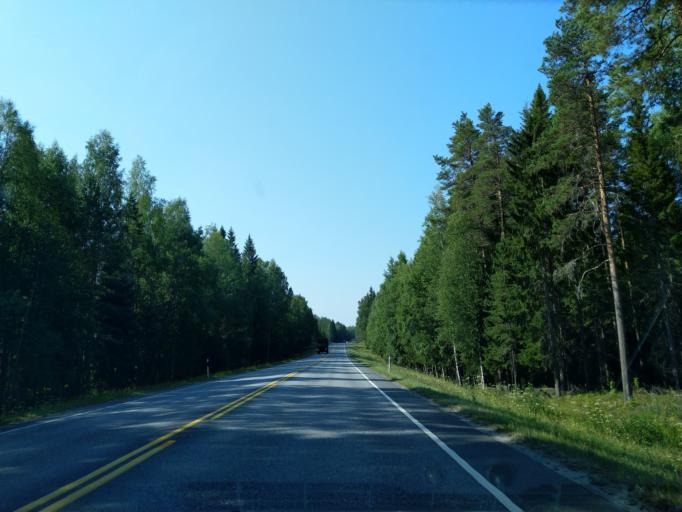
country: FI
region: Satakunta
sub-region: Pori
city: Pomarkku
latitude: 61.6454
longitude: 21.9514
